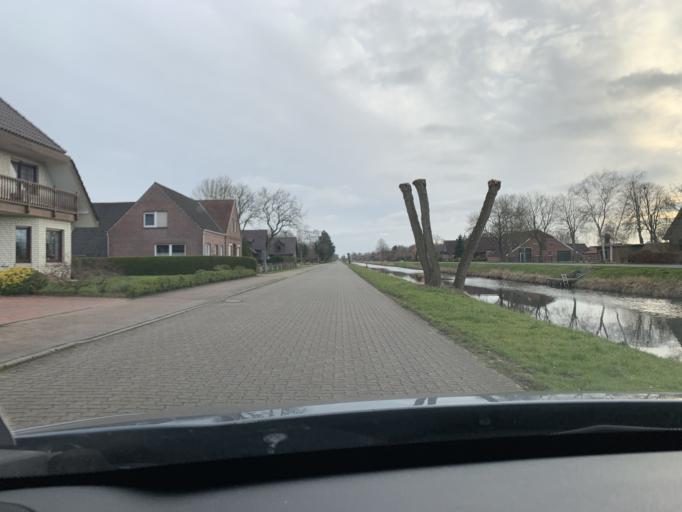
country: DE
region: Lower Saxony
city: Schwerinsdorf
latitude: 53.2766
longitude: 7.7049
